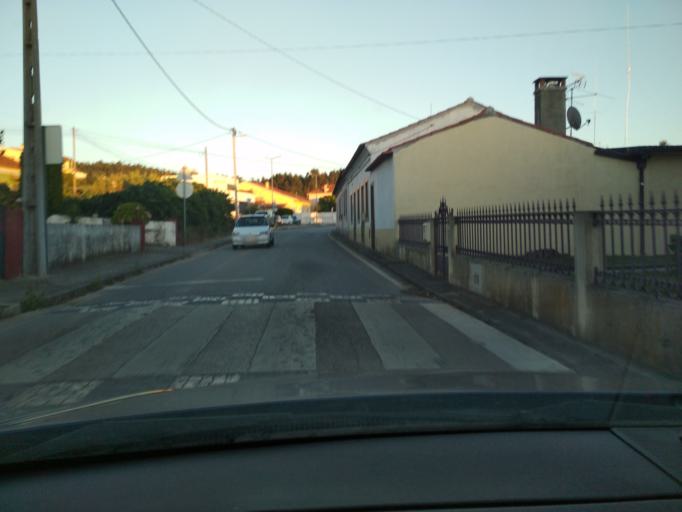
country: PT
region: Coimbra
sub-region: Condeixa-A-Nova
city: Condeixa-a-Nova
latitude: 40.1755
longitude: -8.4842
